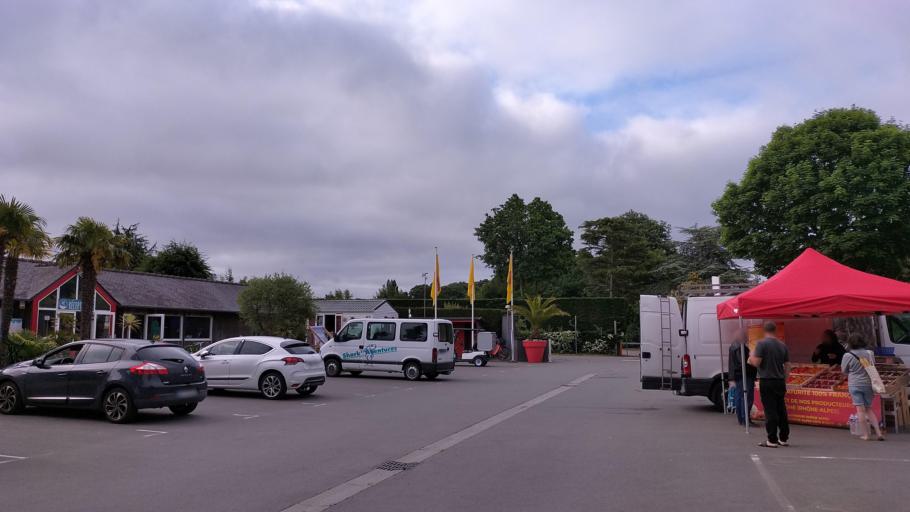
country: FR
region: Brittany
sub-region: Departement d'Ille-et-Vilaine
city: Saint-Jouan-des-Guerets
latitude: 48.6100
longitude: -1.9871
